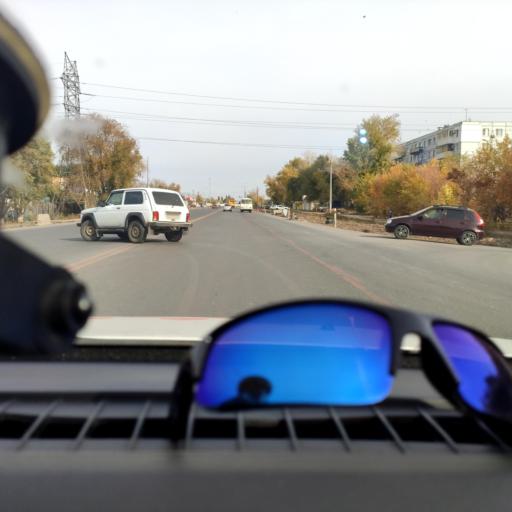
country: RU
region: Samara
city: Samara
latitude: 53.1244
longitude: 50.0889
